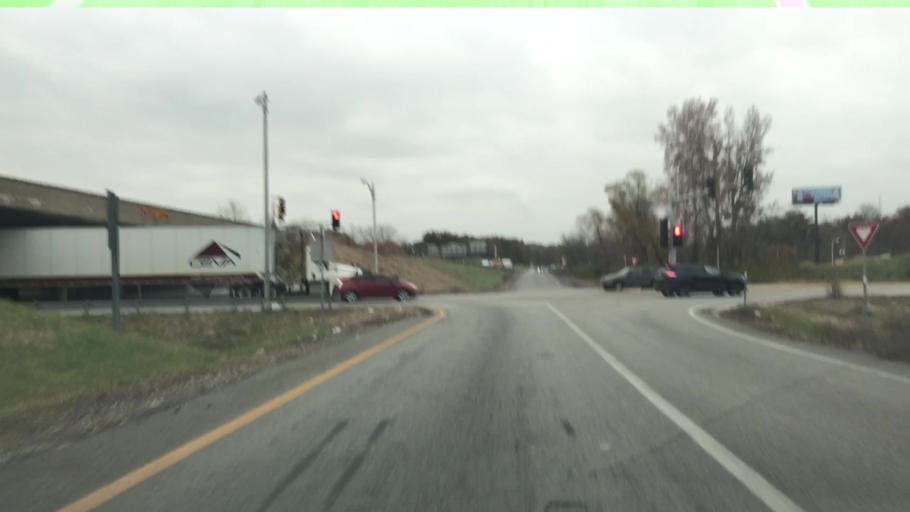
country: US
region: Missouri
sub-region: Clay County
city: Claycomo
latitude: 39.2028
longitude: -94.4933
